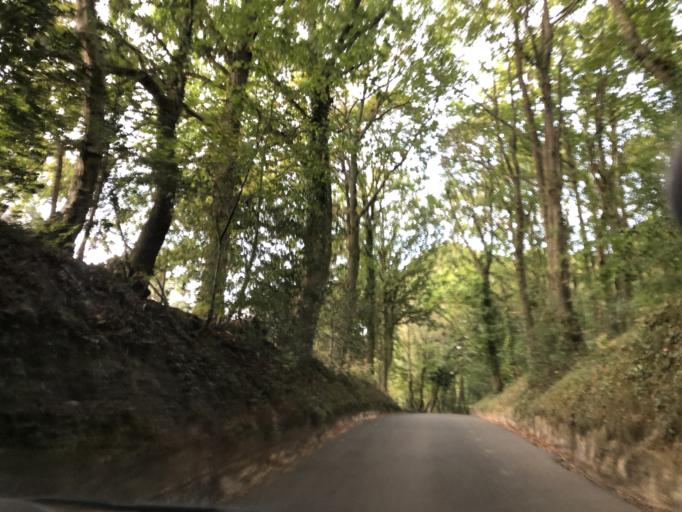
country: GB
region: England
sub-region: East Sussex
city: Bexhill-on-Sea
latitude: 50.8586
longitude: 0.4365
